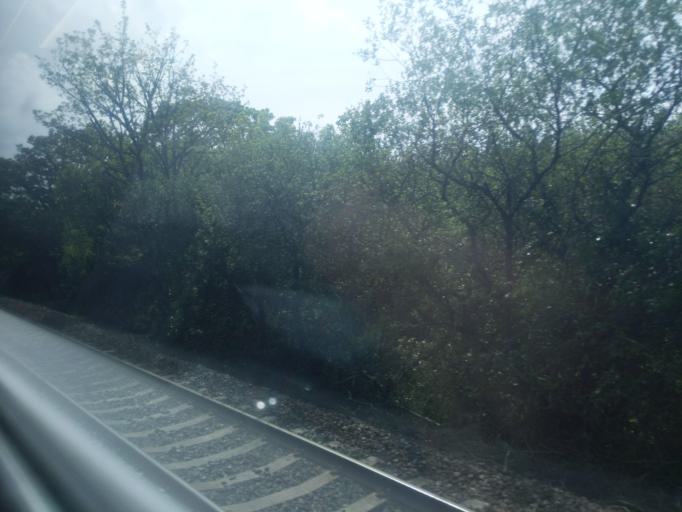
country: GB
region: England
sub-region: Cornwall
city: Marazion
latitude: 50.1431
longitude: -5.4666
